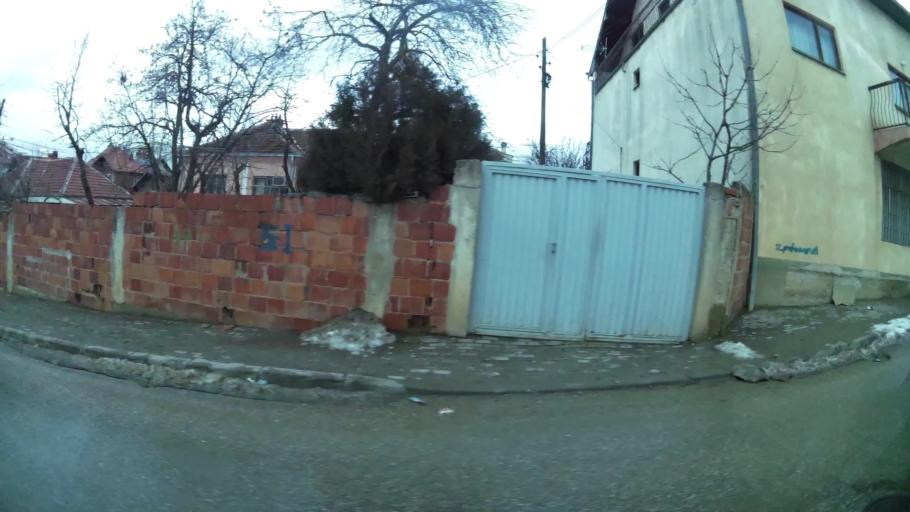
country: XK
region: Pristina
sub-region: Komuna e Prishtines
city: Pristina
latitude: 42.6415
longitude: 21.1707
